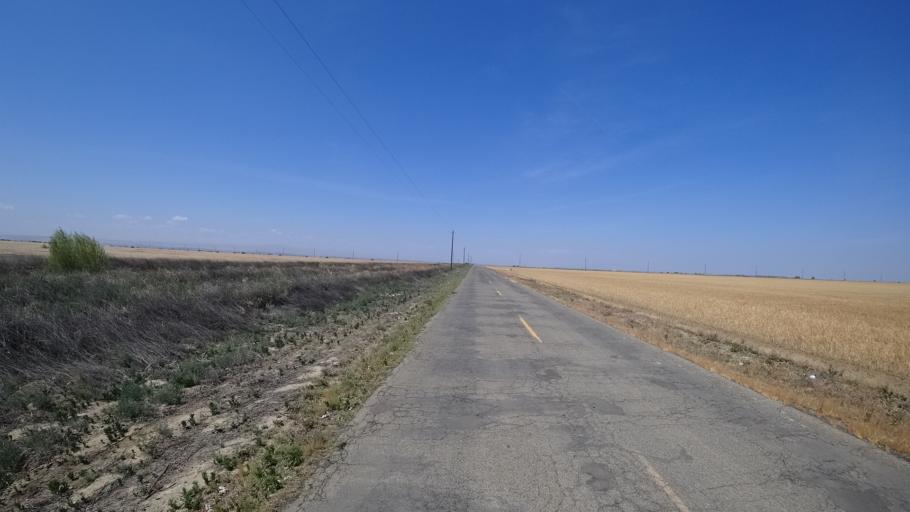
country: US
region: California
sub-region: Kings County
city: Stratford
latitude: 36.1378
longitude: -119.8995
